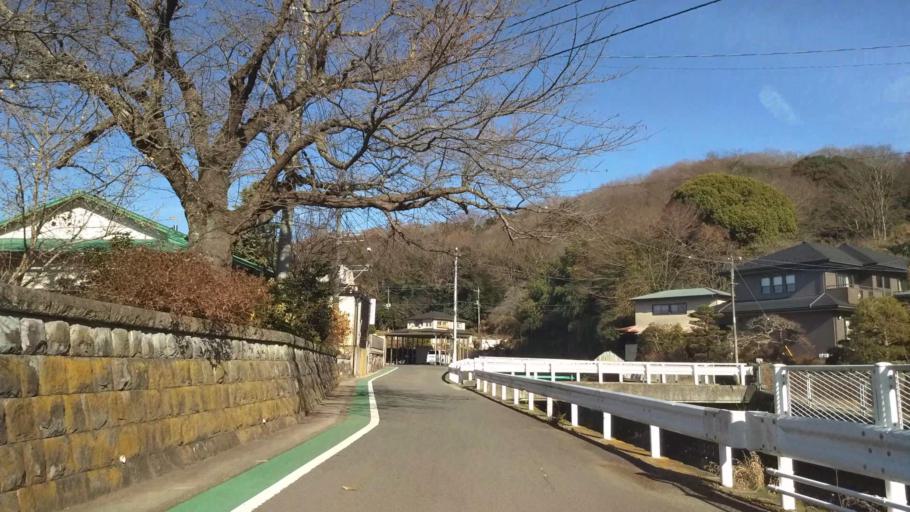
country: JP
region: Kanagawa
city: Ninomiya
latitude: 35.3336
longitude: 139.2352
